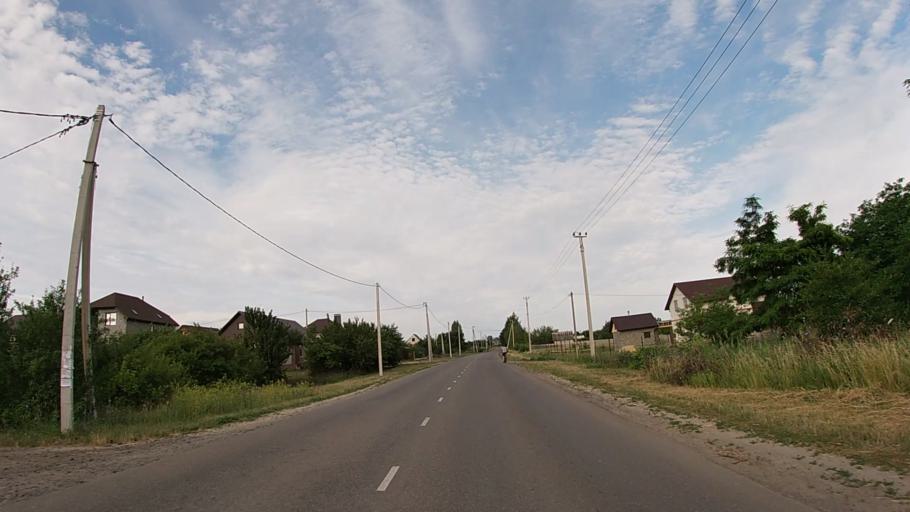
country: RU
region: Belgorod
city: Severnyy
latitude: 50.6943
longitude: 36.5700
